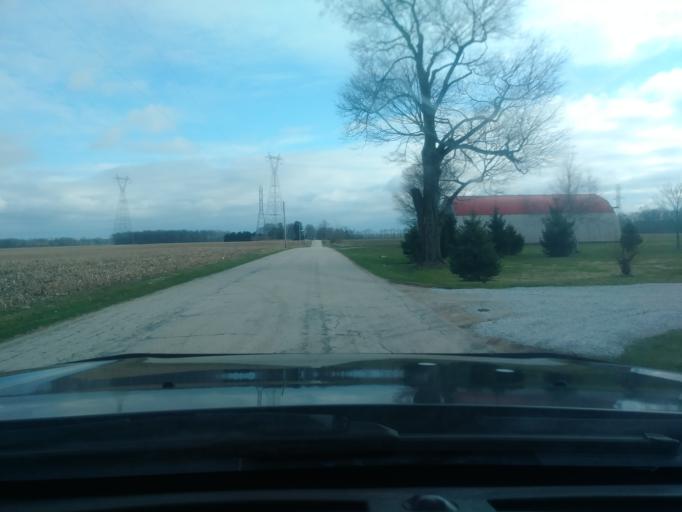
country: US
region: Indiana
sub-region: LaPorte County
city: LaPorte
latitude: 41.5522
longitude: -86.7986
